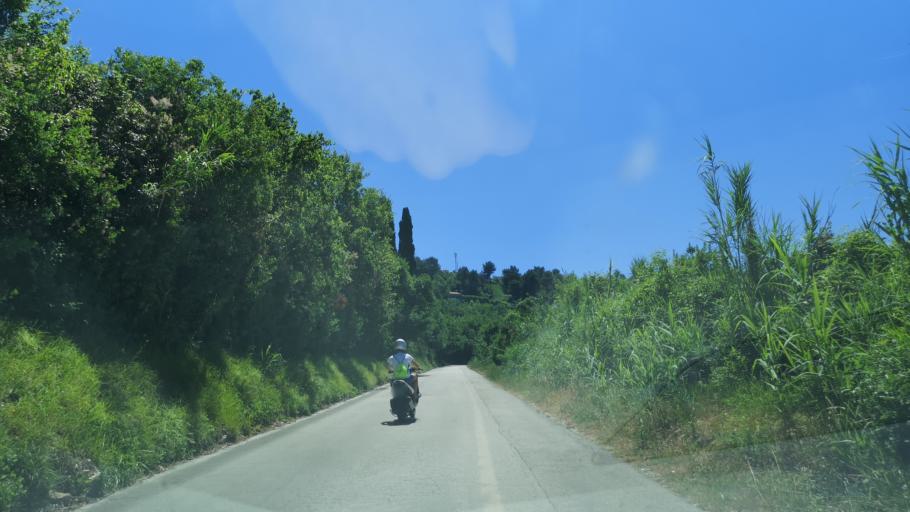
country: SI
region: Piran-Pirano
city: Portoroz
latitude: 45.5246
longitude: 13.5924
